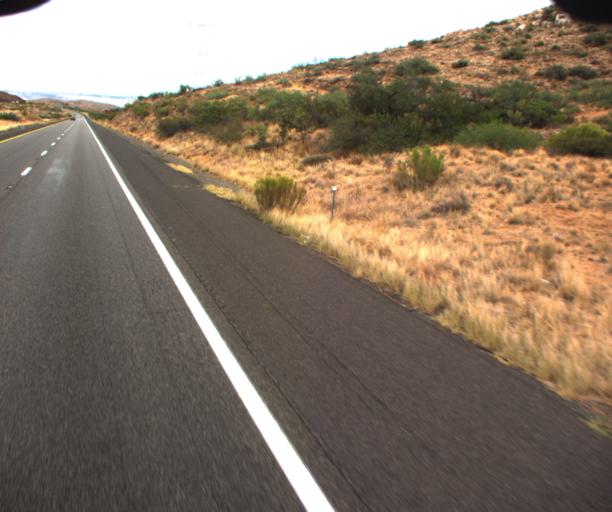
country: US
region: Arizona
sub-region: Yavapai County
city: Cordes Lakes
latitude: 34.2963
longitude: -112.1269
